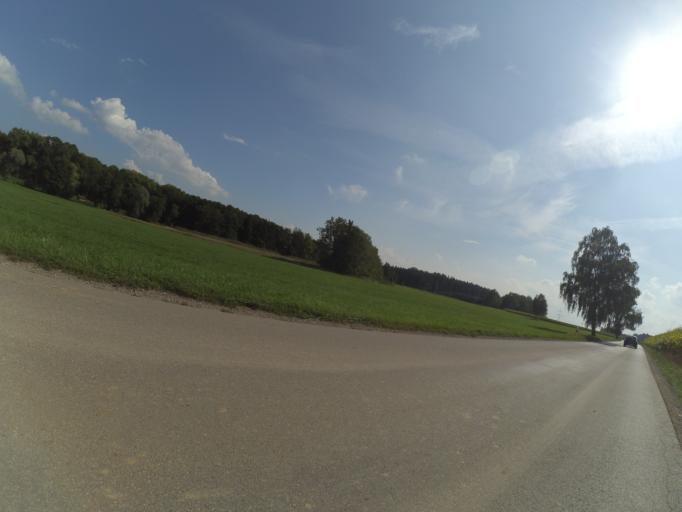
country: DE
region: Bavaria
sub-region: Swabia
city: Lamerdingen
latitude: 48.0786
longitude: 10.7671
